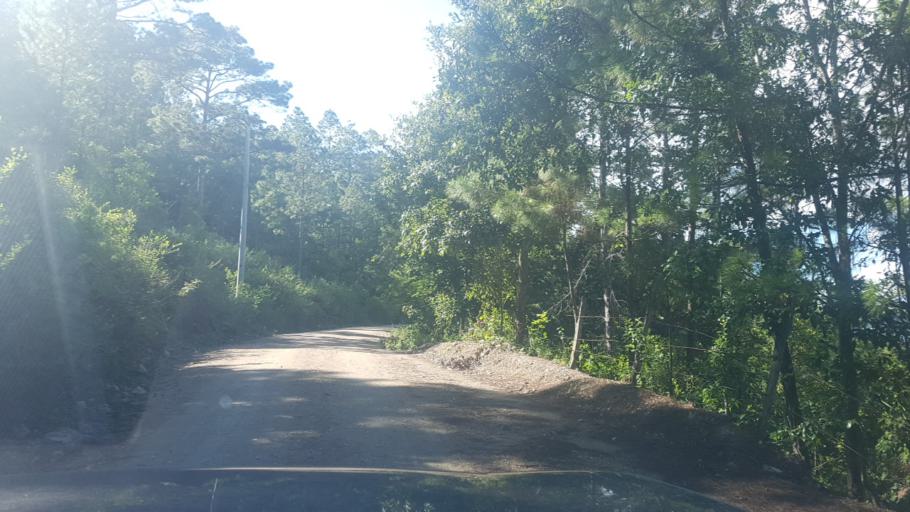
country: NI
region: Nueva Segovia
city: Ocotal
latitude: 13.6421
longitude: -86.6354
